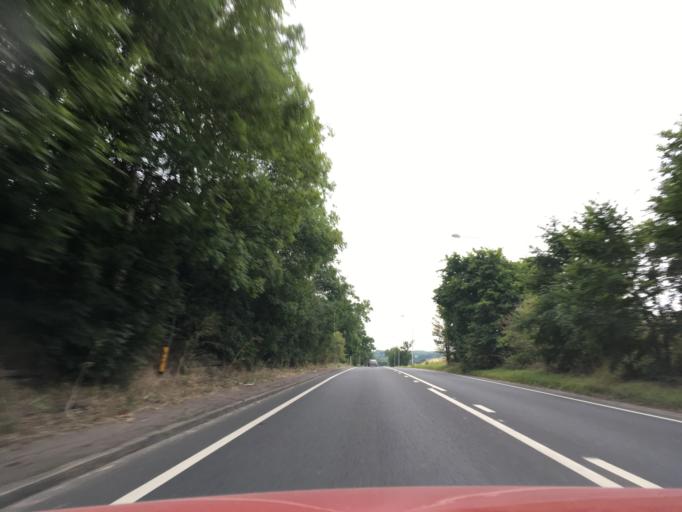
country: GB
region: England
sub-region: Central Bedfordshire
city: Hockliffe
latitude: 51.9195
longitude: -0.5689
